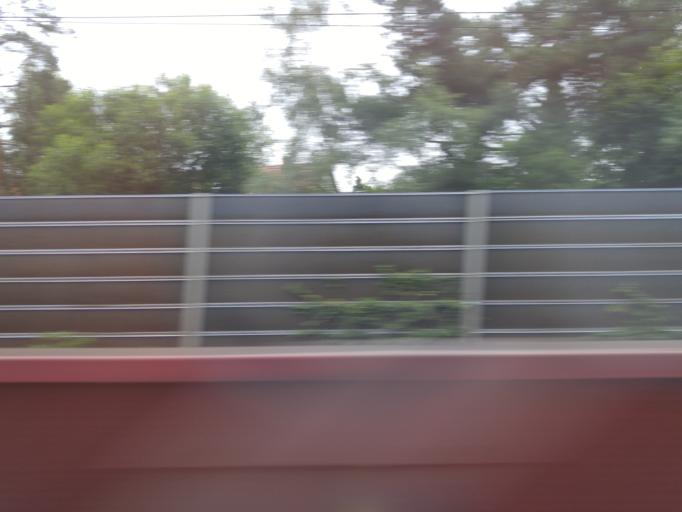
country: DE
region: Hesse
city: Langen
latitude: 49.9867
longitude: 8.6559
